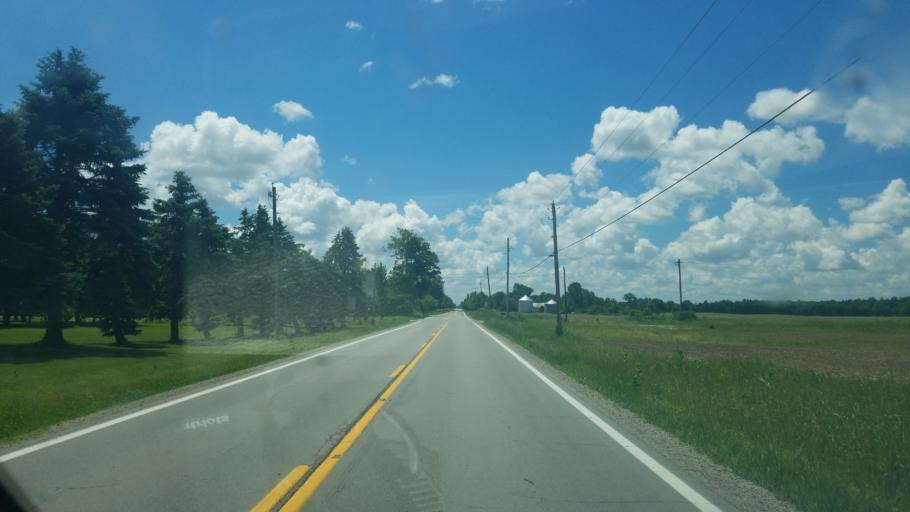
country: US
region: Ohio
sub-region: Huron County
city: Wakeman
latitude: 41.1754
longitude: -82.4106
